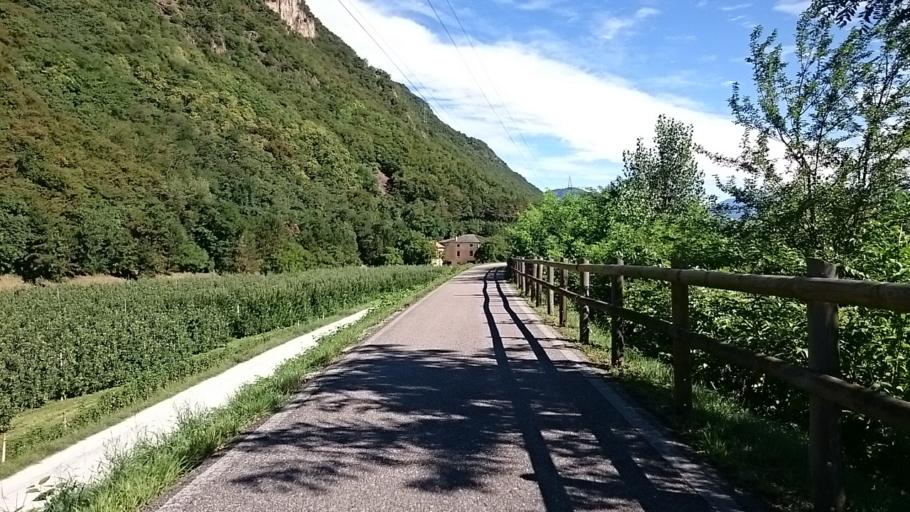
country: IT
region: Trentino-Alto Adige
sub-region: Bolzano
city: Vadena
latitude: 46.4266
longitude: 11.3100
